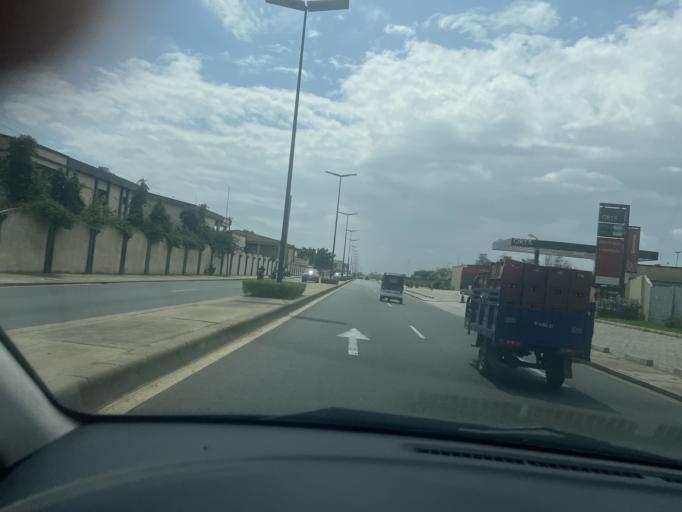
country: BJ
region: Littoral
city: Cotonou
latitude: 6.3497
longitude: 2.3857
